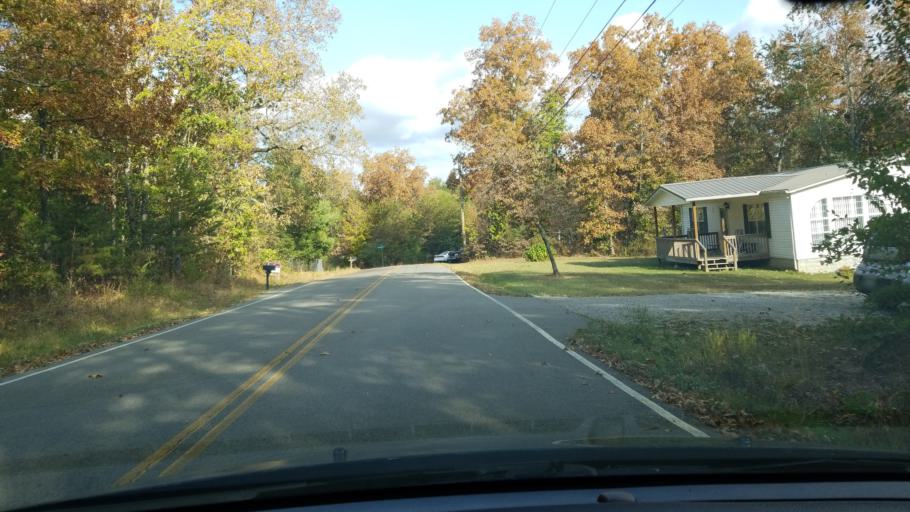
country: US
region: Tennessee
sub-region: Cumberland County
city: Crossville
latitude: 35.9484
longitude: -85.0506
